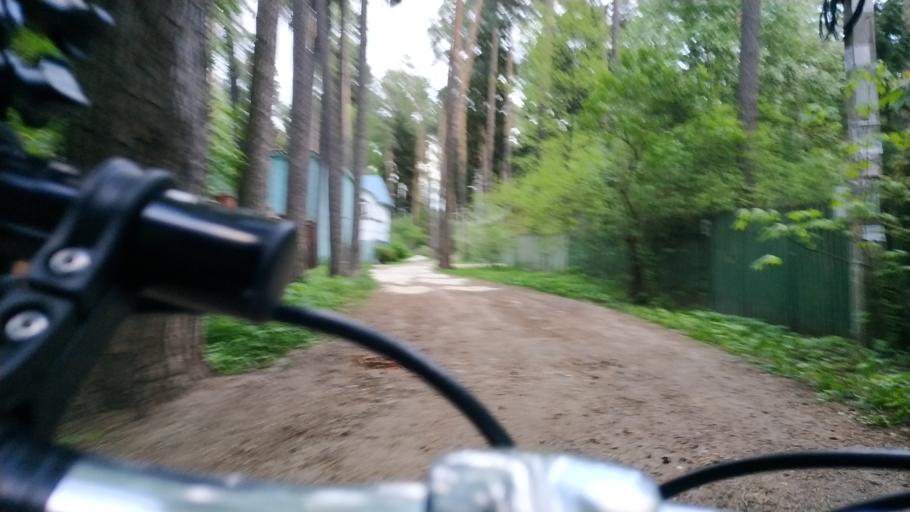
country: RU
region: Moskovskaya
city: Kratovo
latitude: 55.6083
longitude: 38.1573
